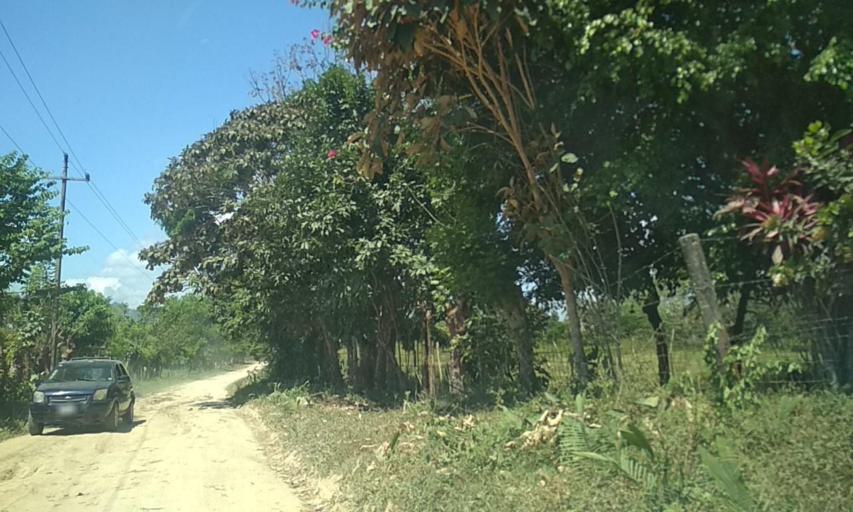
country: MX
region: Veracruz
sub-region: Moloacan
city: Cuichapa
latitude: 17.7866
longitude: -94.1910
